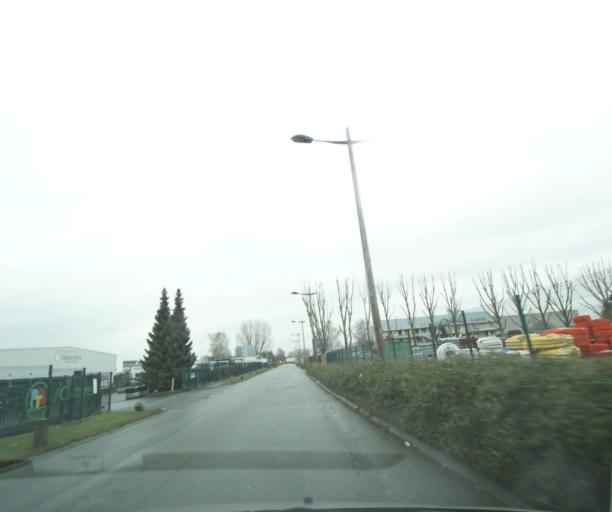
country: FR
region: Nord-Pas-de-Calais
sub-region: Departement du Nord
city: Prouvy
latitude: 50.3323
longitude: 3.4483
